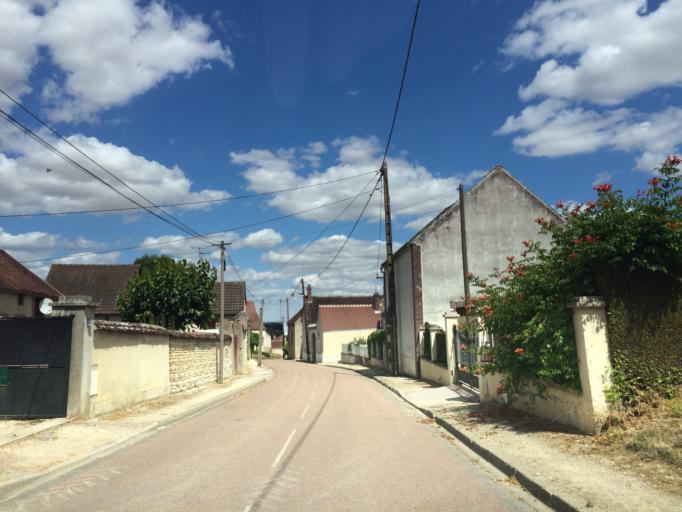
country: FR
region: Bourgogne
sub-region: Departement de l'Yonne
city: Laroche-Saint-Cydroine
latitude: 47.9377
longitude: 3.4857
